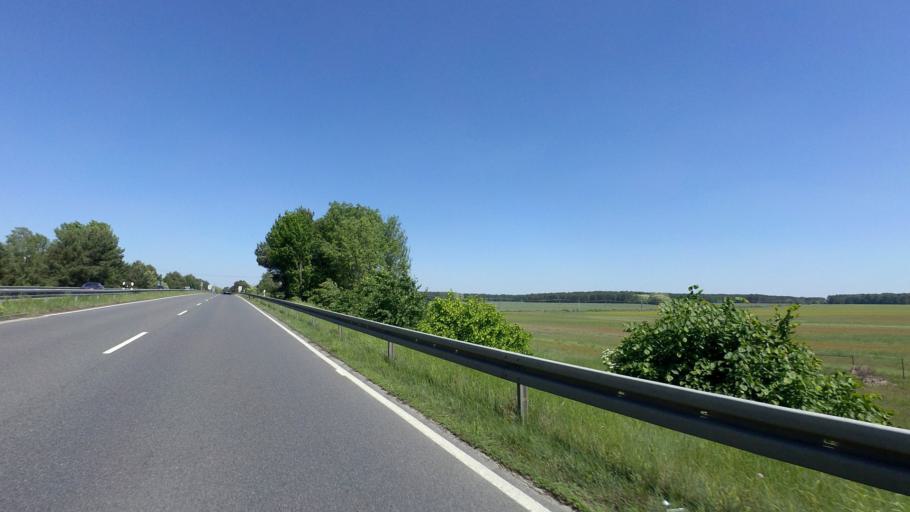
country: DE
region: Brandenburg
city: Cottbus
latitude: 51.6863
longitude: 14.3593
